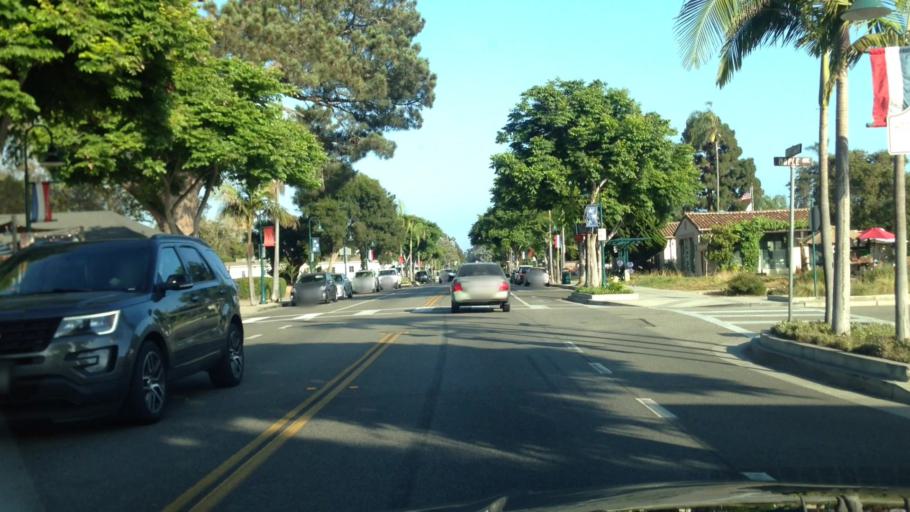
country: US
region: California
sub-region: Santa Barbara County
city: Carpinteria
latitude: 34.3982
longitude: -119.5176
